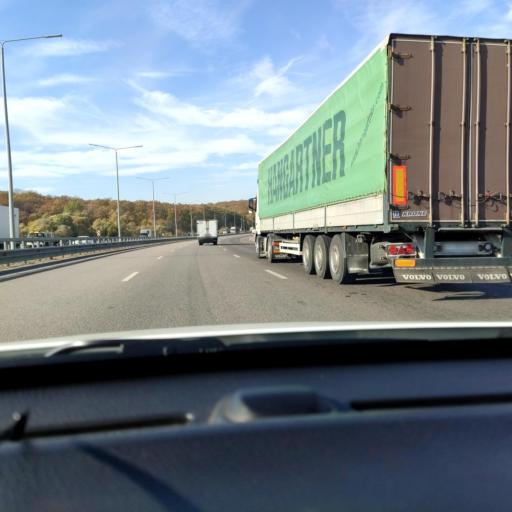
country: RU
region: Voronezj
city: Somovo
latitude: 51.7949
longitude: 39.2616
